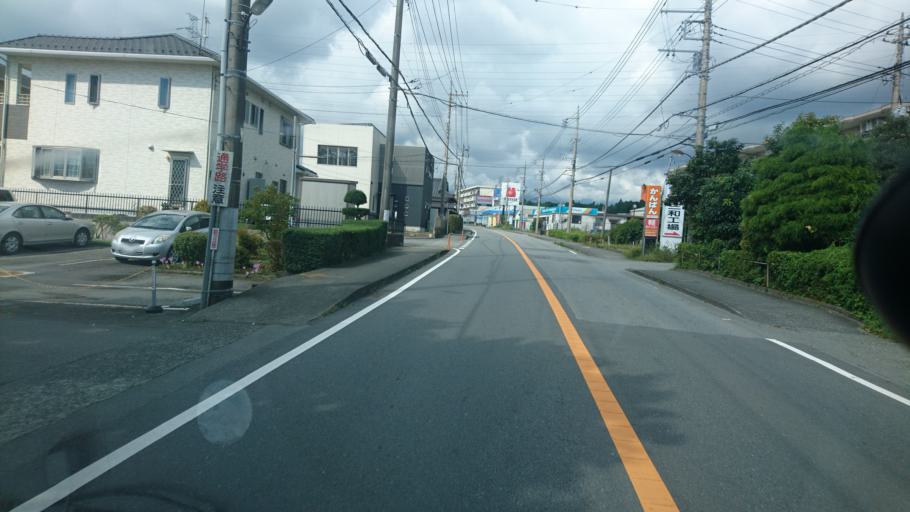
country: JP
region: Shizuoka
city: Gotemba
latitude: 35.3070
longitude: 138.9168
